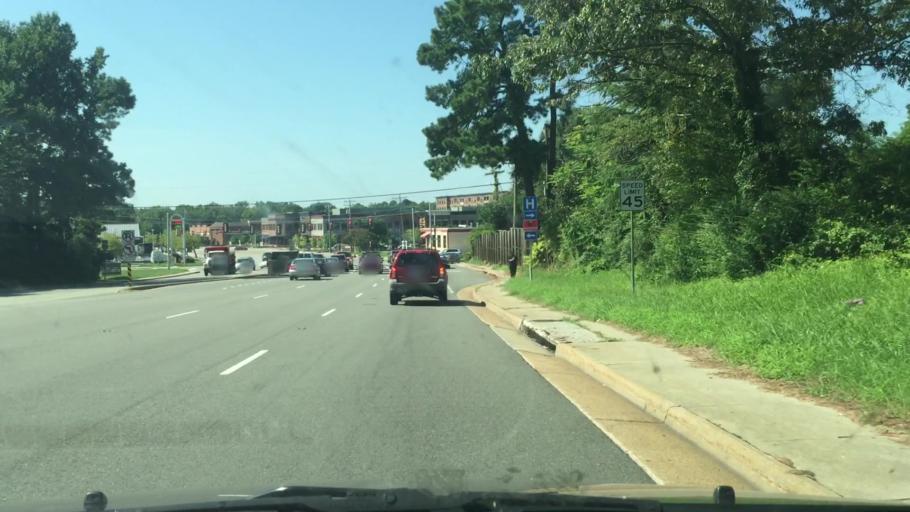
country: US
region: Virginia
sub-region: Henrico County
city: Dumbarton
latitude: 37.5938
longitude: -77.4929
